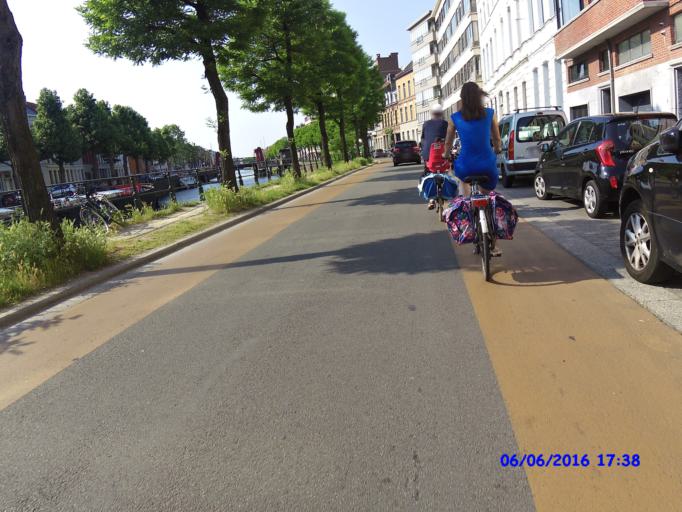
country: BE
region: Flanders
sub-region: Provincie Oost-Vlaanderen
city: Ledeberg
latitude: 51.0476
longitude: 3.7392
